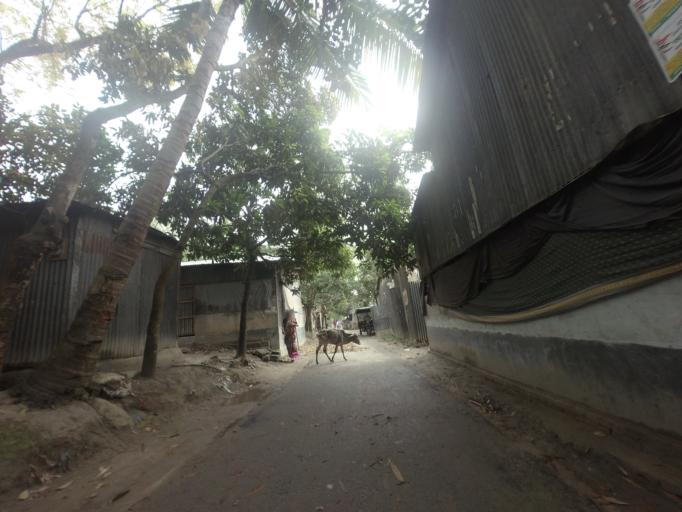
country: BD
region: Rajshahi
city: Sirajganj
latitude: 24.3272
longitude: 89.6966
